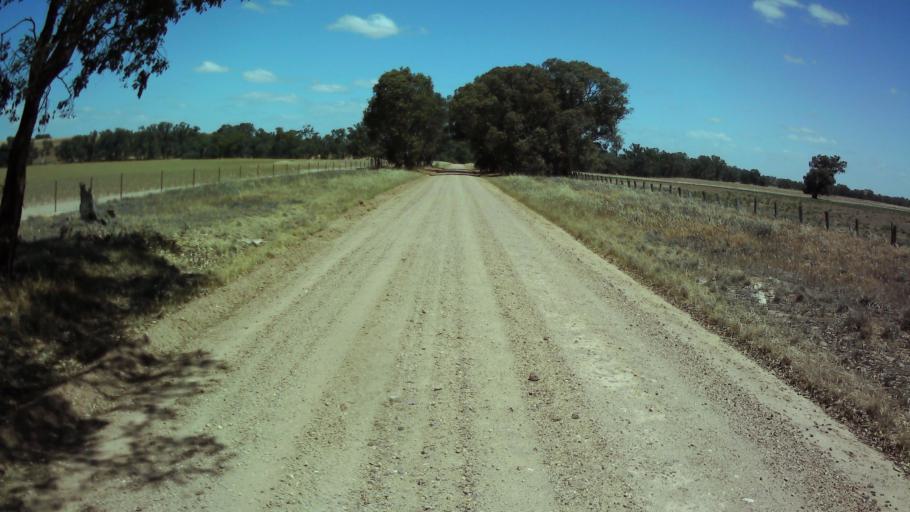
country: AU
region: New South Wales
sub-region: Weddin
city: Grenfell
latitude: -33.9286
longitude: 148.3349
